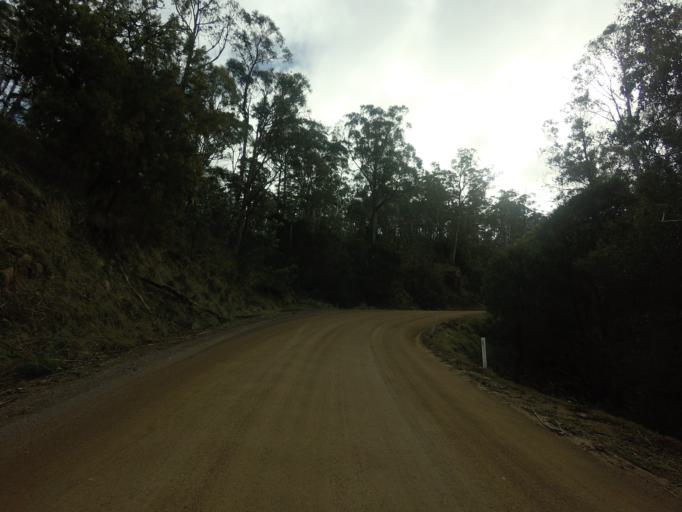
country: AU
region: Tasmania
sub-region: Derwent Valley
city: New Norfolk
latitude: -42.7421
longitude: 146.8665
